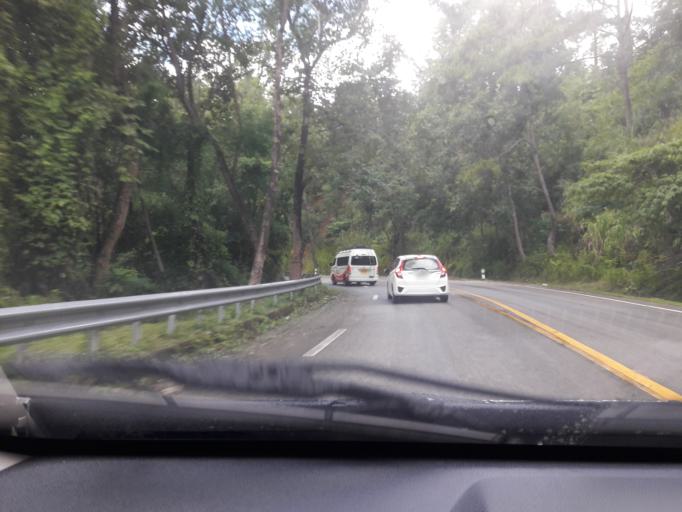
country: TH
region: Mae Hong Son
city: Mae Hi
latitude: 19.2311
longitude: 98.6695
